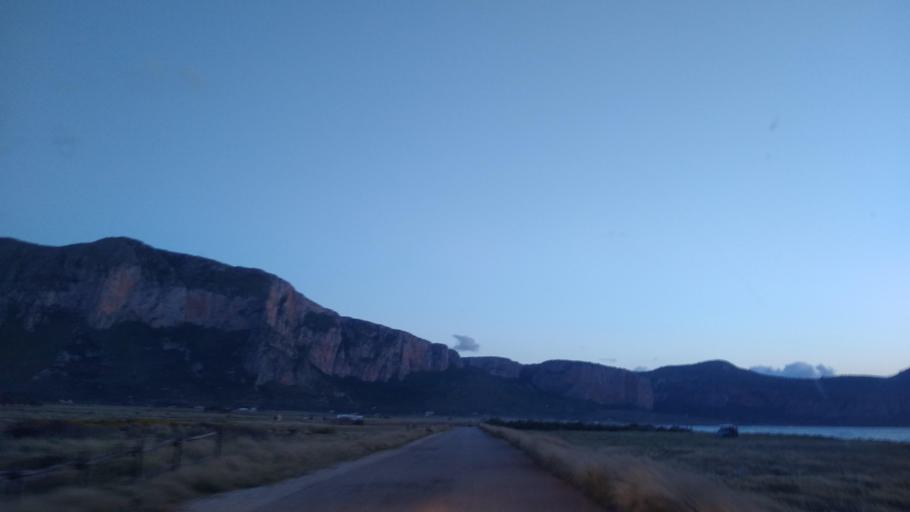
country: IT
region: Sicily
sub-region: Trapani
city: Castelluzzo
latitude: 38.1195
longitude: 12.7227
